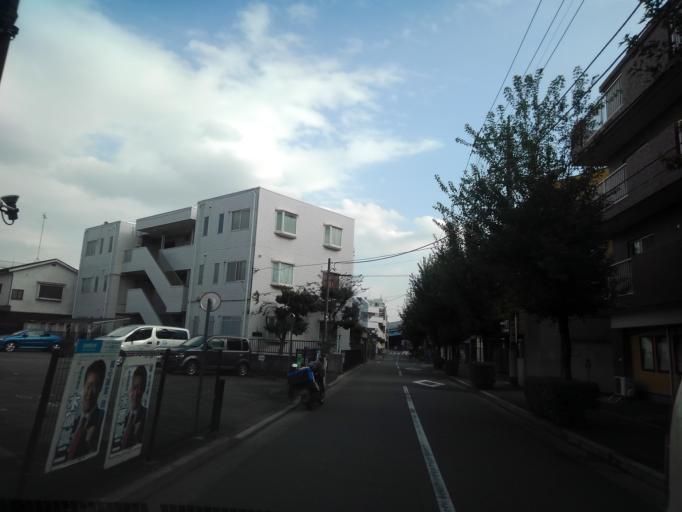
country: JP
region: Tokyo
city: Higashimurayama-shi
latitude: 35.7524
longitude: 139.4701
